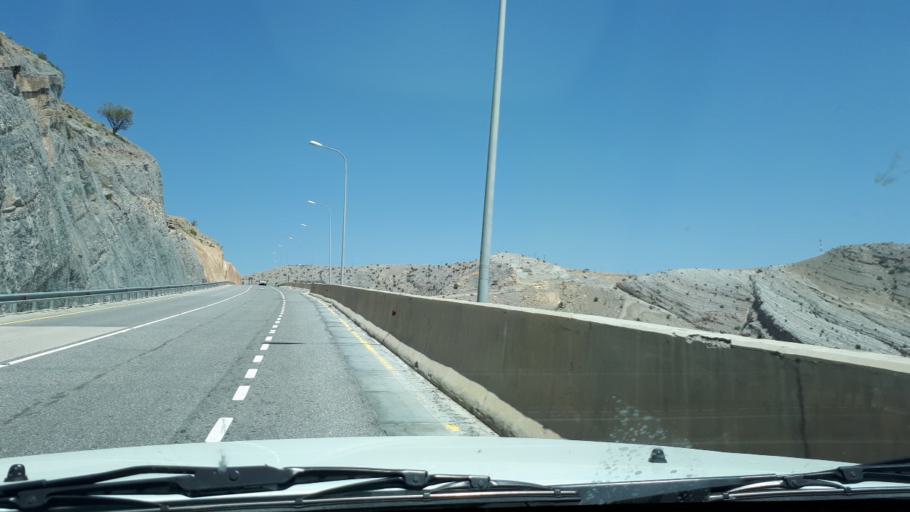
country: OM
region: Muhafazat ad Dakhiliyah
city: Izki
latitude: 23.0130
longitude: 57.6977
